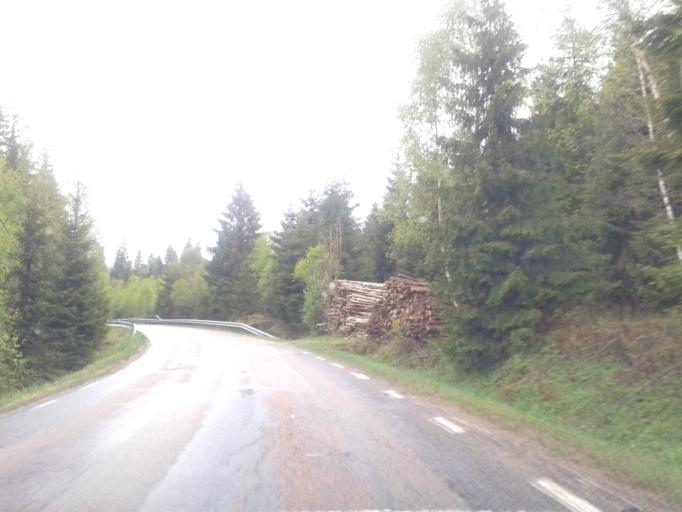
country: SE
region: Vaestra Goetaland
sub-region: Lilla Edets Kommun
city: Lilla Edet
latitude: 58.0916
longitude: 12.0695
